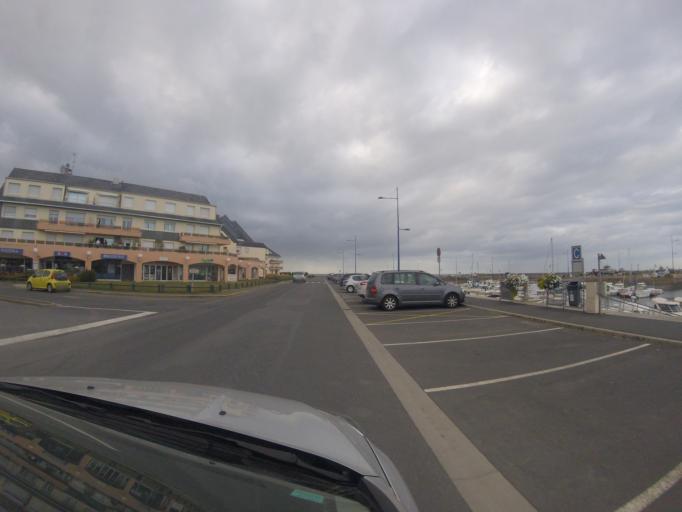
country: FR
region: Lower Normandy
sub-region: Departement du Calvados
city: Grandcamp-Maisy
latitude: 49.3881
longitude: -1.0505
